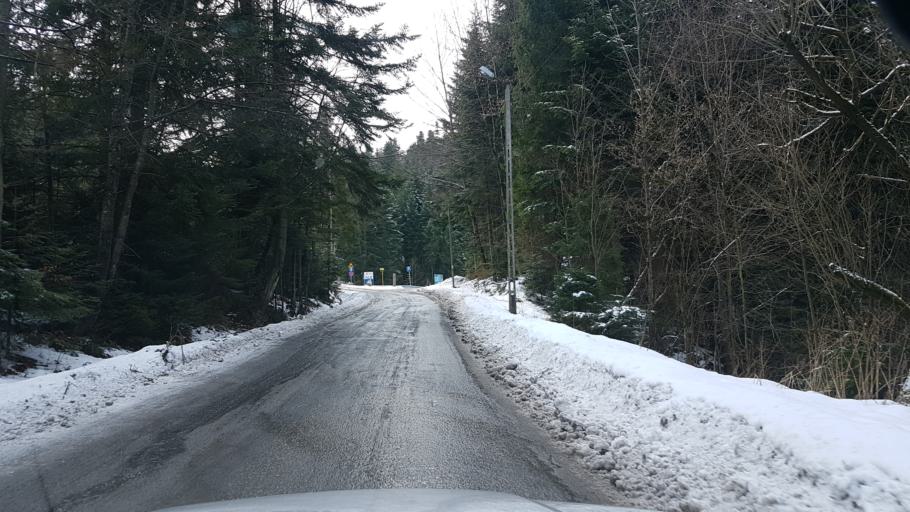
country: PL
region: Lesser Poland Voivodeship
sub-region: Powiat nowosadecki
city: Piwniczna-Zdroj
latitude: 49.4195
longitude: 20.6468
